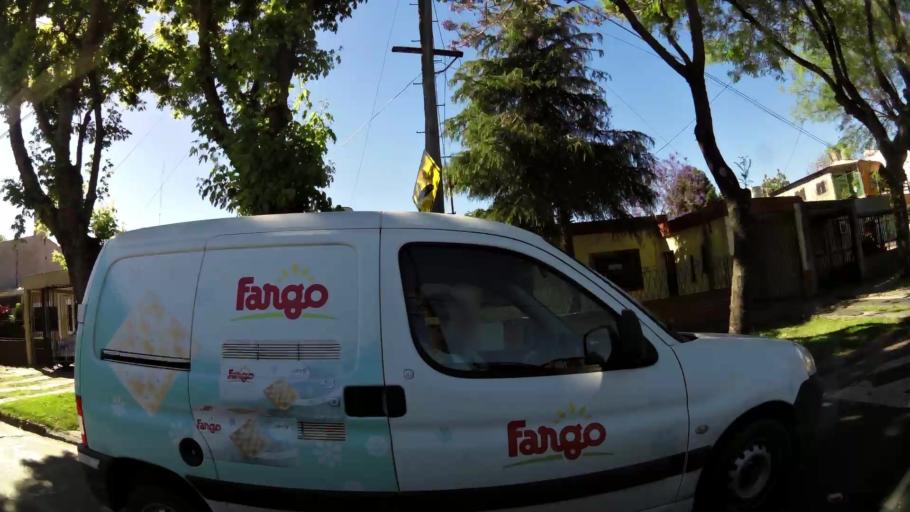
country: AR
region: Buenos Aires
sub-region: Partido de General San Martin
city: General San Martin
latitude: -34.5461
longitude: -58.5225
